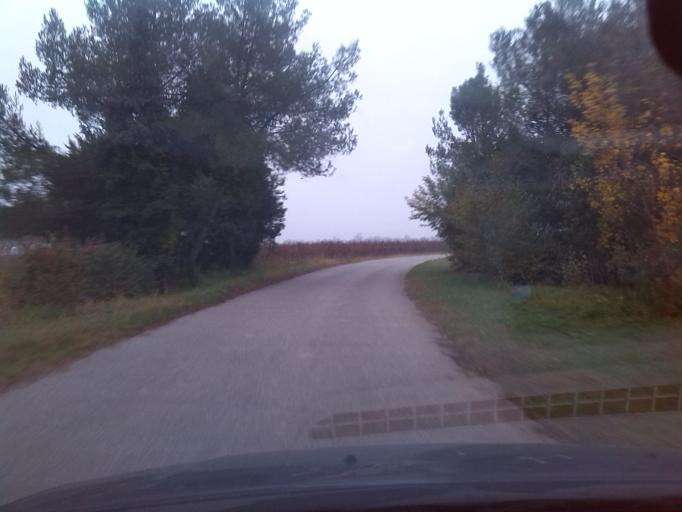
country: IT
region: Friuli Venezia Giulia
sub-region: Provincia di Gorizia
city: Moraro
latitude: 45.9154
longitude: 13.4855
